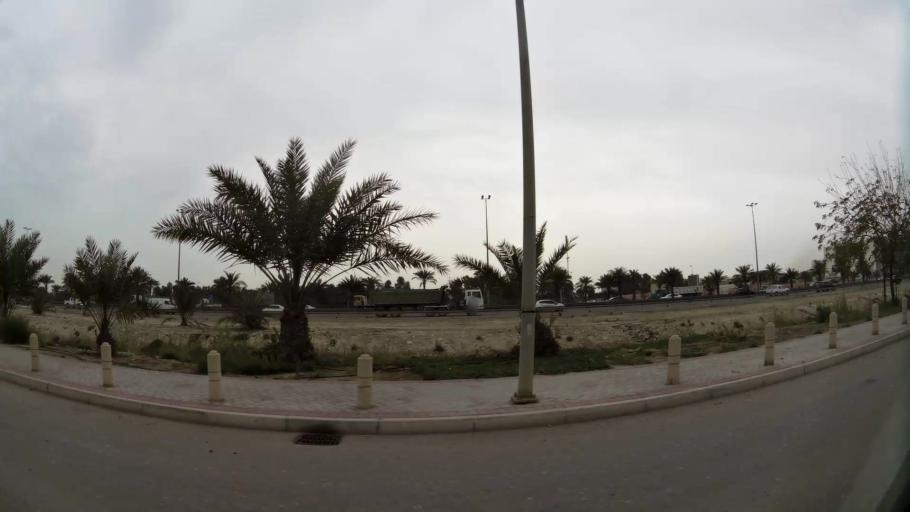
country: BH
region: Manama
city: Jidd Hafs
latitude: 26.1977
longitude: 50.5475
